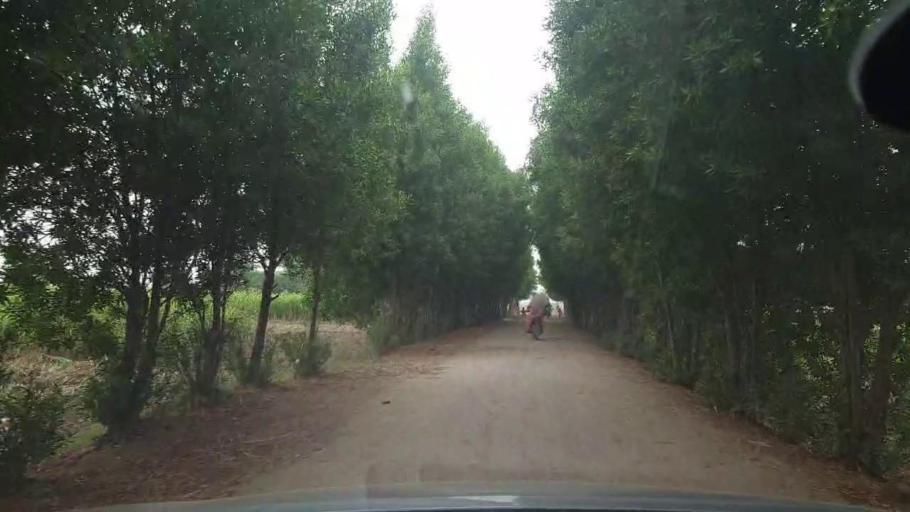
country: PK
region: Sindh
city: Jacobabad
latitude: 28.2903
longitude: 68.4184
